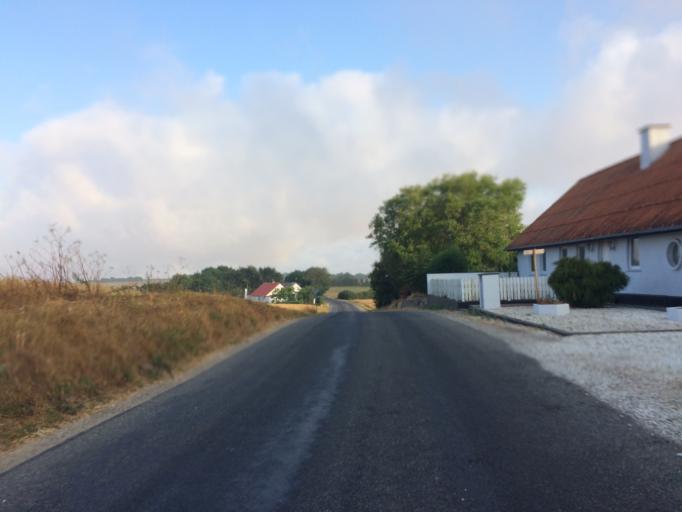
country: DK
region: Central Jutland
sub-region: Holstebro Kommune
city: Vinderup
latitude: 56.5902
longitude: 8.7555
